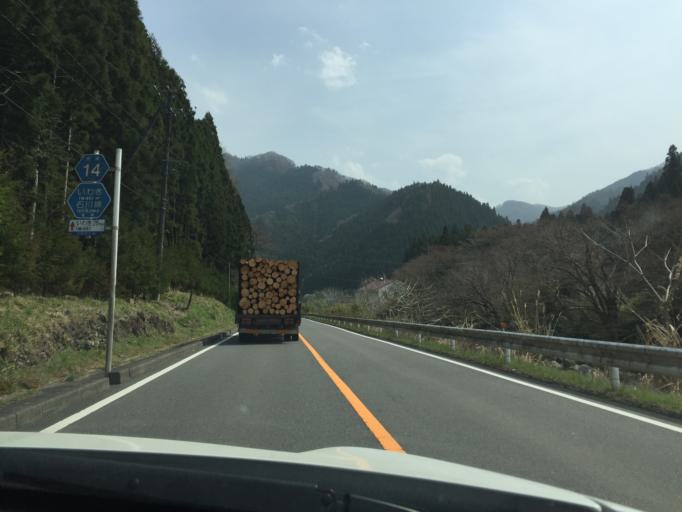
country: JP
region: Fukushima
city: Ishikawa
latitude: 37.0393
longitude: 140.6210
